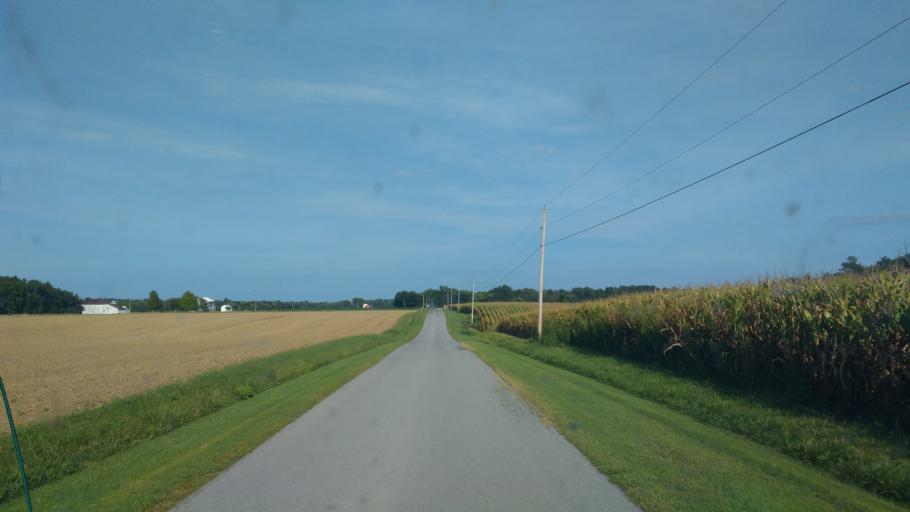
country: US
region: Ohio
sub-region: Wyandot County
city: Upper Sandusky
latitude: 40.8466
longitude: -83.3852
